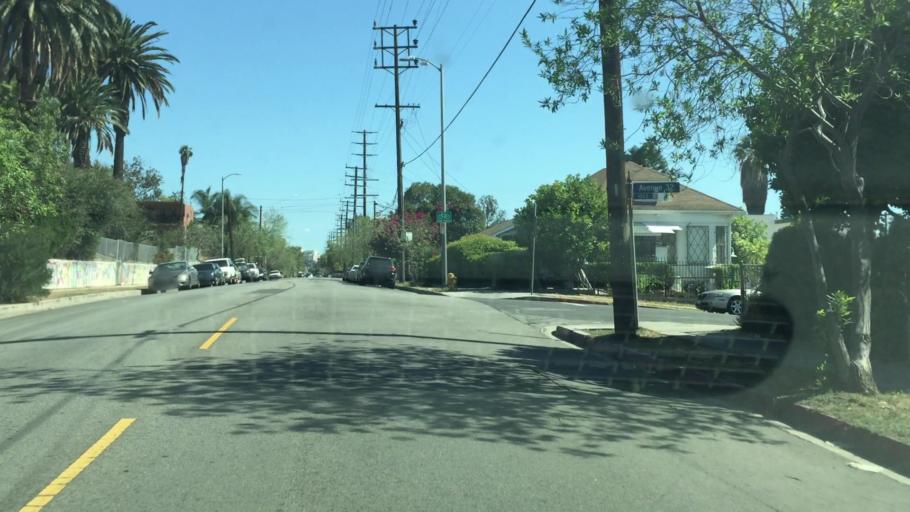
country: US
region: California
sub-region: Los Angeles County
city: Los Angeles
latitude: 34.0822
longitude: -118.2119
